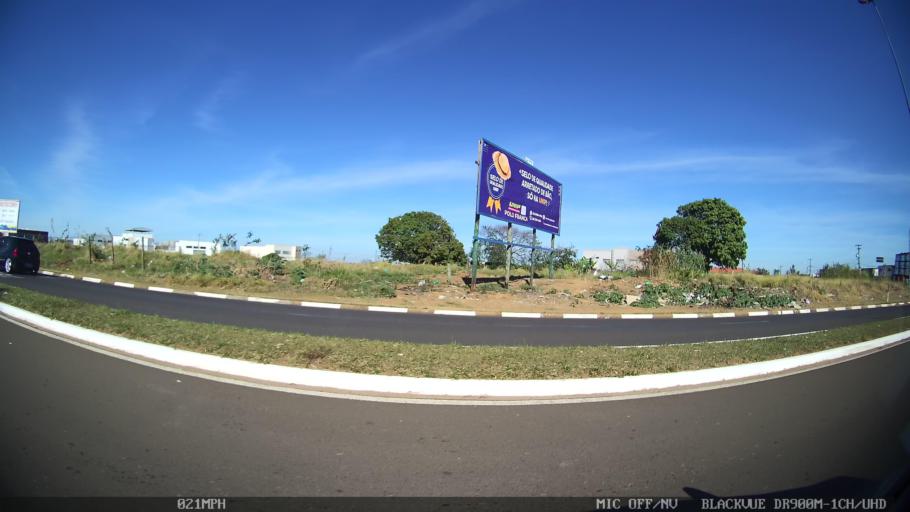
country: BR
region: Sao Paulo
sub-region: Franca
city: Franca
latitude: -20.5385
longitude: -47.3629
